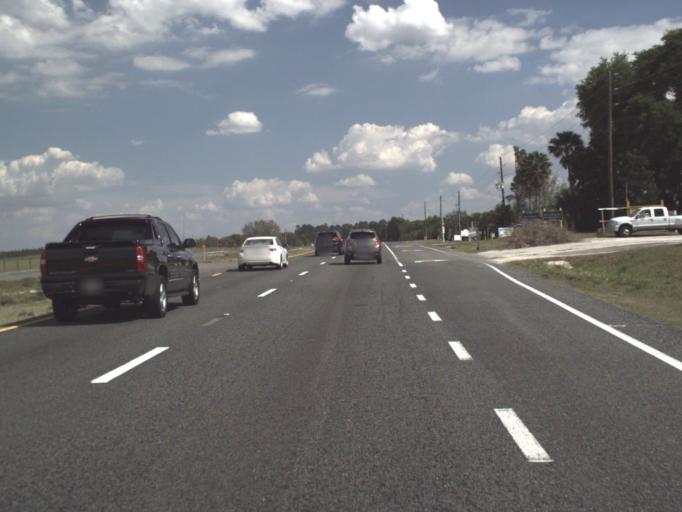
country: US
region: Florida
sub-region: Lake County
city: Mascotte
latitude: 28.6504
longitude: -81.8356
